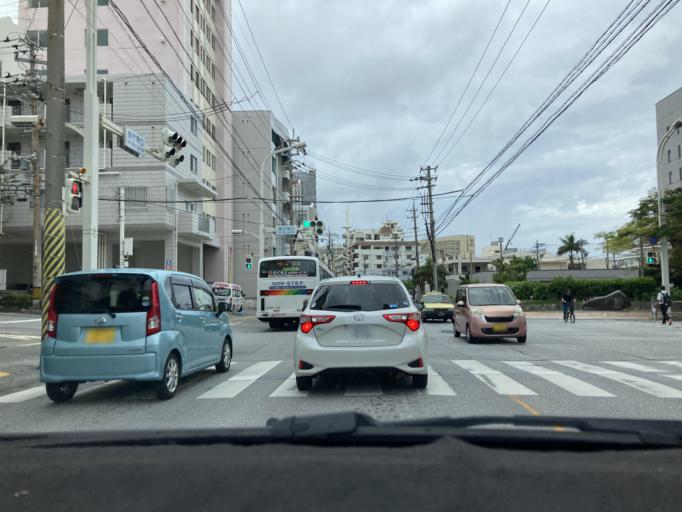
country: JP
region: Okinawa
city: Naha-shi
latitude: 26.2108
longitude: 127.6819
